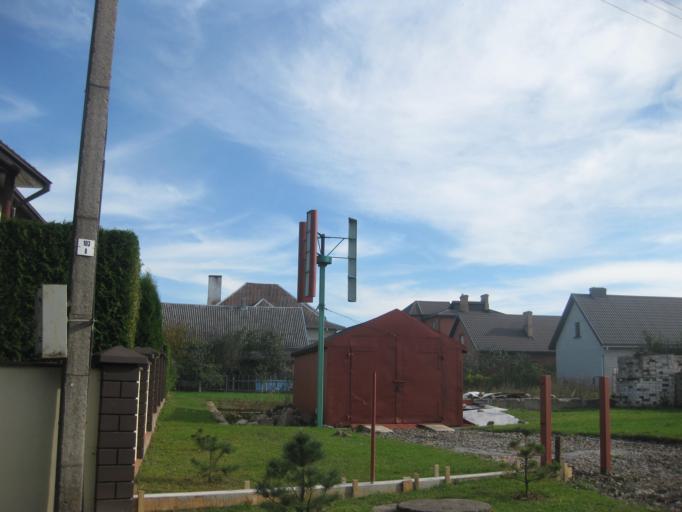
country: LT
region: Kauno apskritis
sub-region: Kauno rajonas
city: Garliava
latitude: 54.8215
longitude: 23.8581
